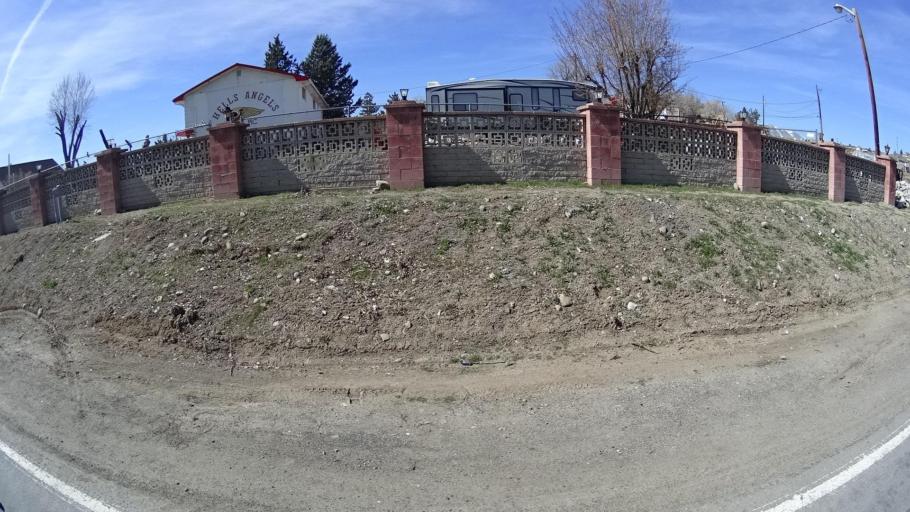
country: US
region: Nevada
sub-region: Washoe County
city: Sparks
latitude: 39.5563
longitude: -119.7719
